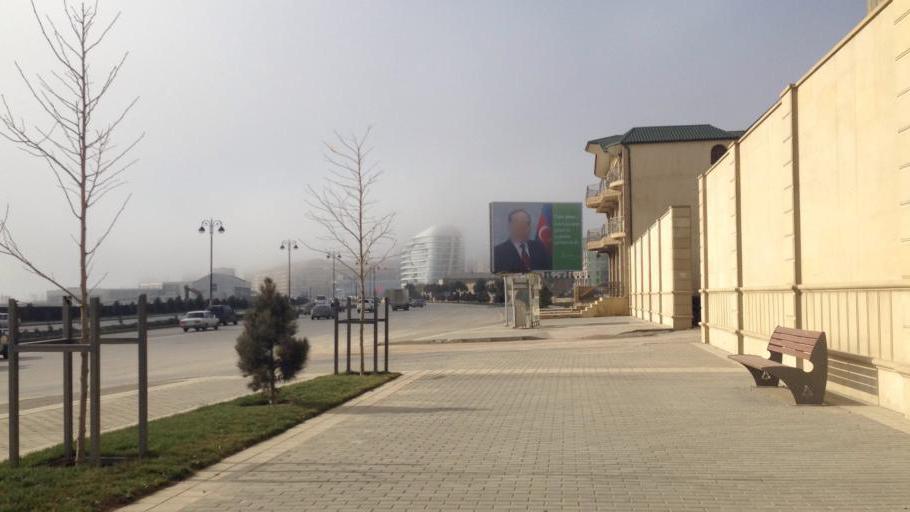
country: AZ
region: Baki
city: Baku
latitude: 40.3786
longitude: 49.8900
